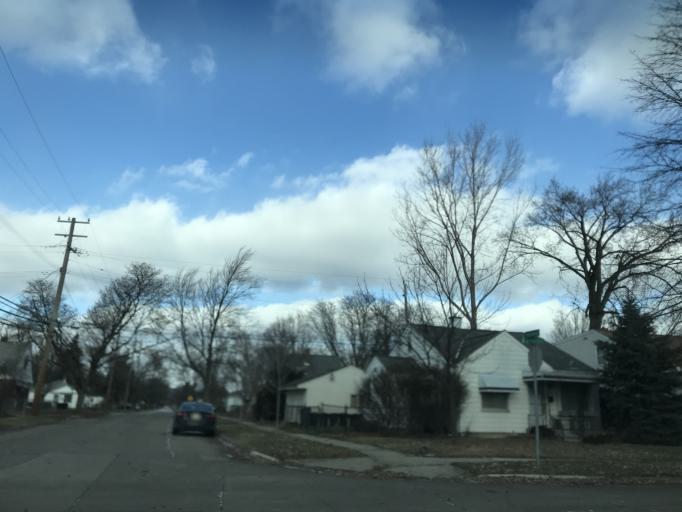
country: US
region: Michigan
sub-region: Oakland County
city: Madison Heights
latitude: 42.4786
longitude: -83.1173
